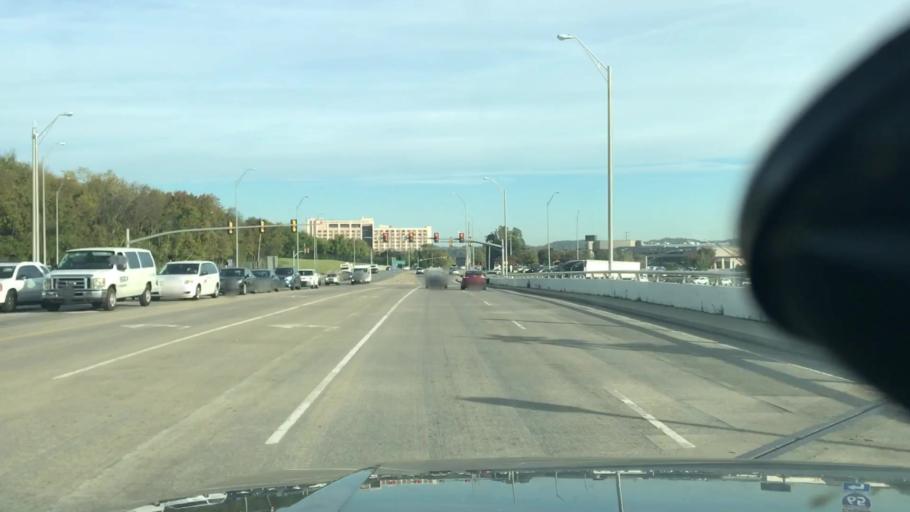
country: US
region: Tennessee
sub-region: Davidson County
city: Nashville
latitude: 36.1839
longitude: -86.7979
